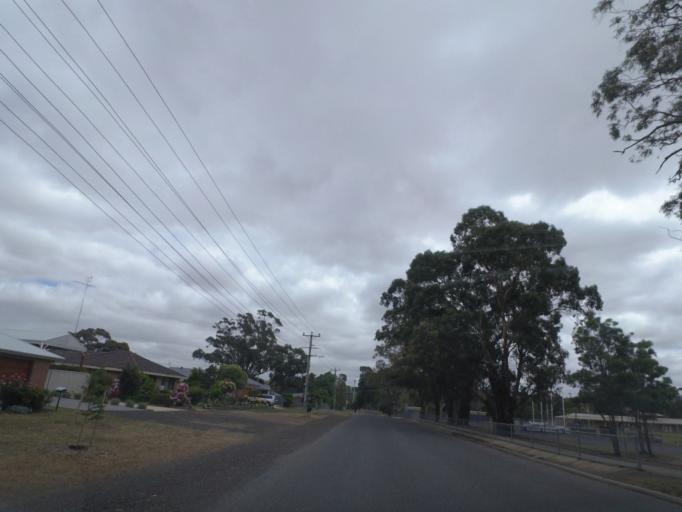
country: AU
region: Victoria
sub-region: Whittlesea
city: Whittlesea
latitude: -37.2042
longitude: 145.0442
